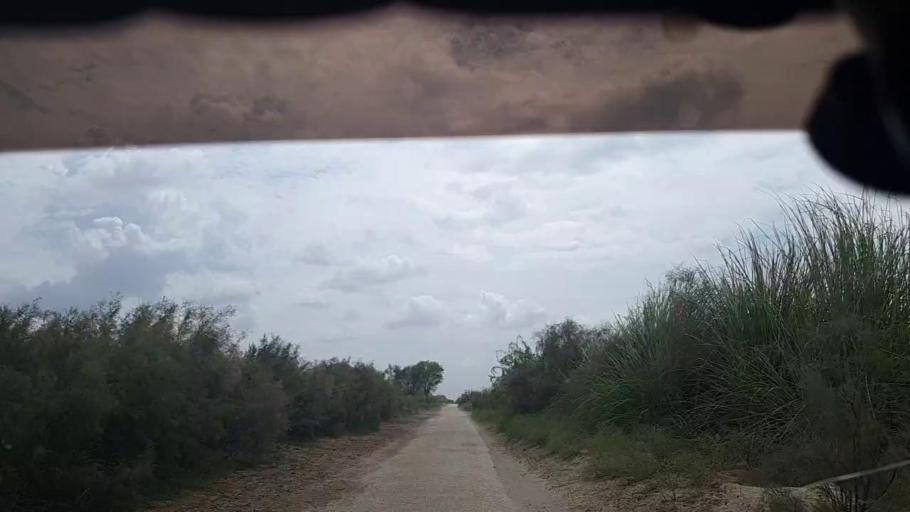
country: PK
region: Sindh
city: Rustam jo Goth
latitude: 28.0357
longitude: 68.9381
